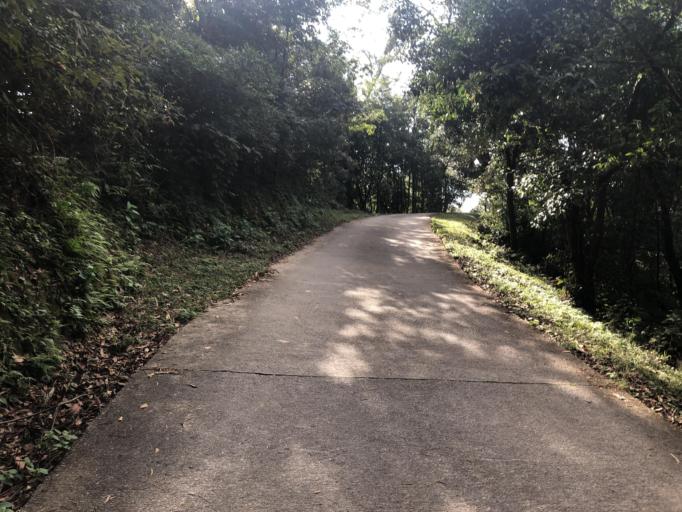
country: HK
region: Tsuen Wan
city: Tsuen Wan
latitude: 22.4030
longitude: 114.0968
